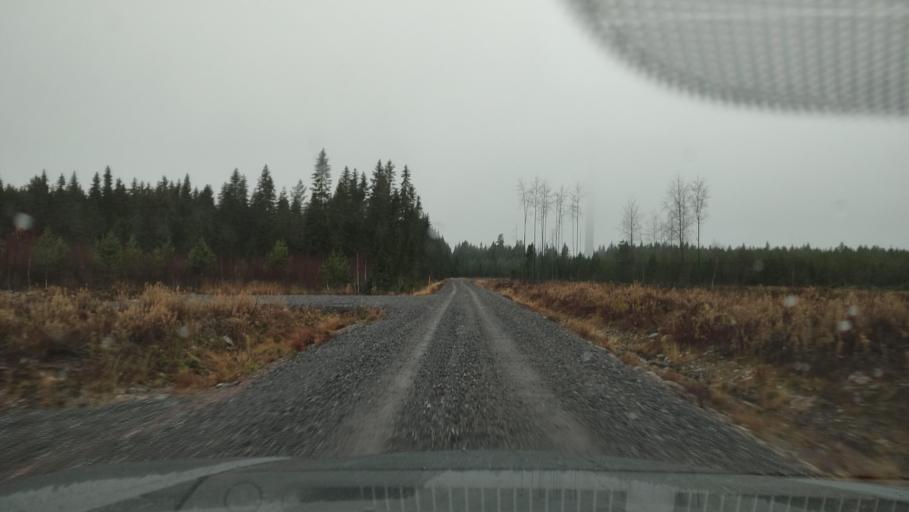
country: FI
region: Southern Ostrobothnia
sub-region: Suupohja
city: Karijoki
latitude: 62.1786
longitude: 21.7223
